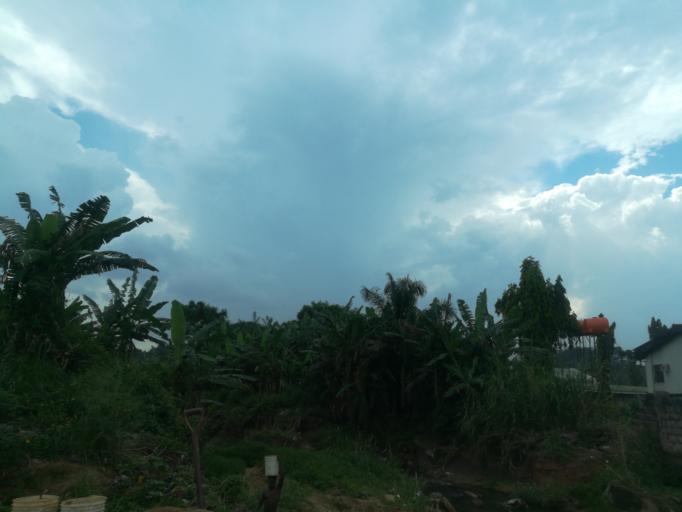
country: NG
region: Oyo
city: Ibadan
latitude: 7.4132
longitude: 3.9034
